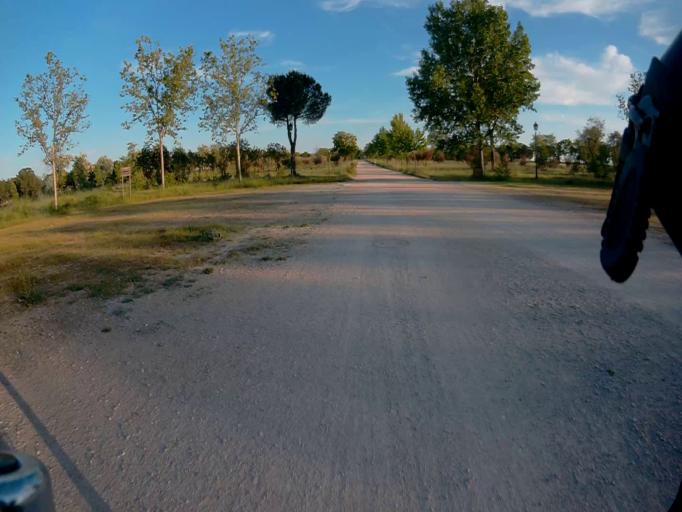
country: ES
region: Madrid
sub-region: Provincia de Madrid
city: Alcorcon
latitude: 40.3223
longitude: -3.8005
